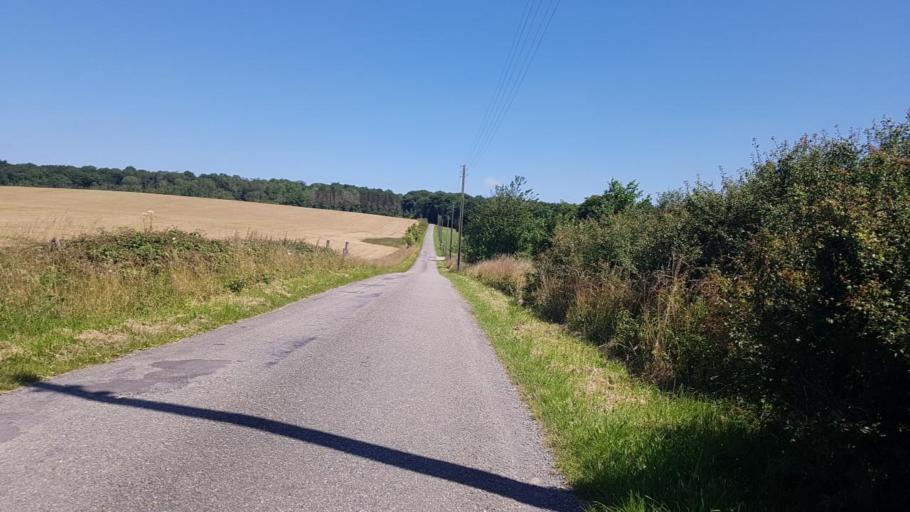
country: BE
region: Wallonia
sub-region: Province du Hainaut
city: Momignies
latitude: 50.0995
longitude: 4.2285
